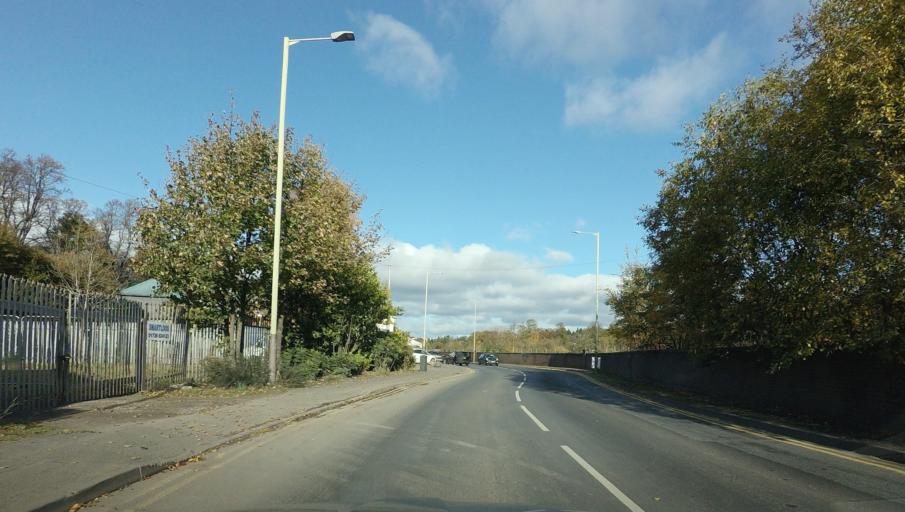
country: GB
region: Scotland
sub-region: Perth and Kinross
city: Perth
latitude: 56.3870
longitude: -3.4268
